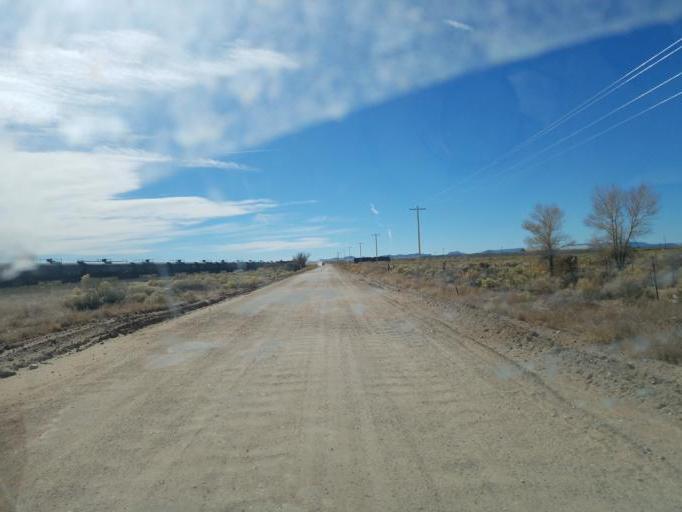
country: US
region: Colorado
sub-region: Costilla County
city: San Luis
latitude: 37.4315
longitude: -105.5245
